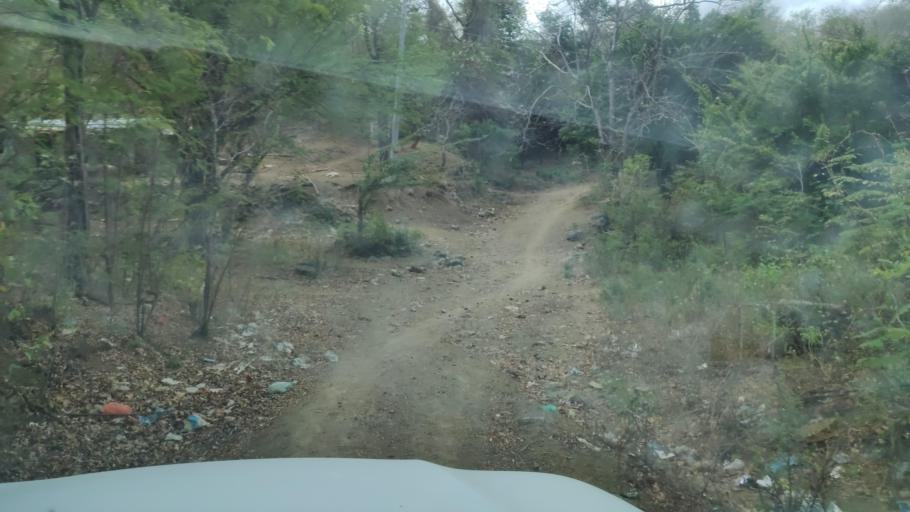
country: NI
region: Carazo
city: Santa Teresa
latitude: 11.6393
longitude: -86.2214
